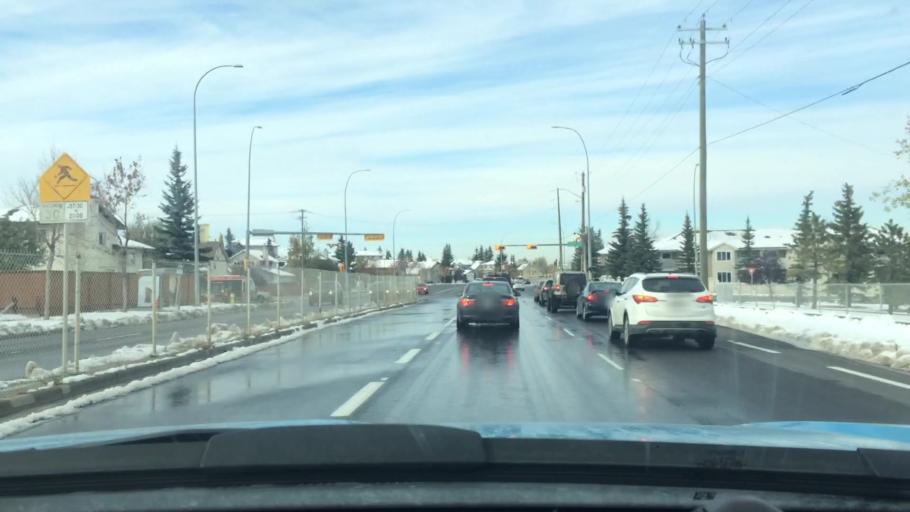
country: CA
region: Alberta
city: Calgary
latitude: 51.1395
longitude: -114.1085
